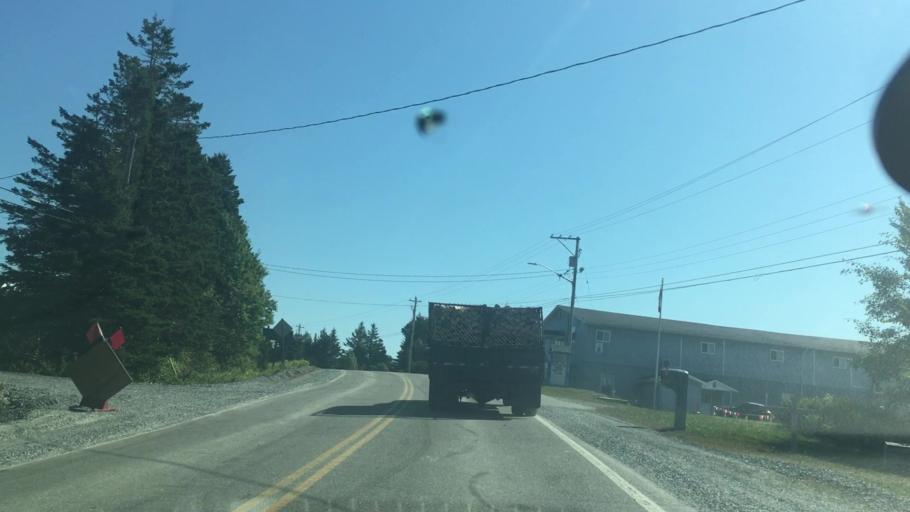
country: CA
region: Nova Scotia
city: New Glasgow
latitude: 44.9051
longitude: -62.4875
